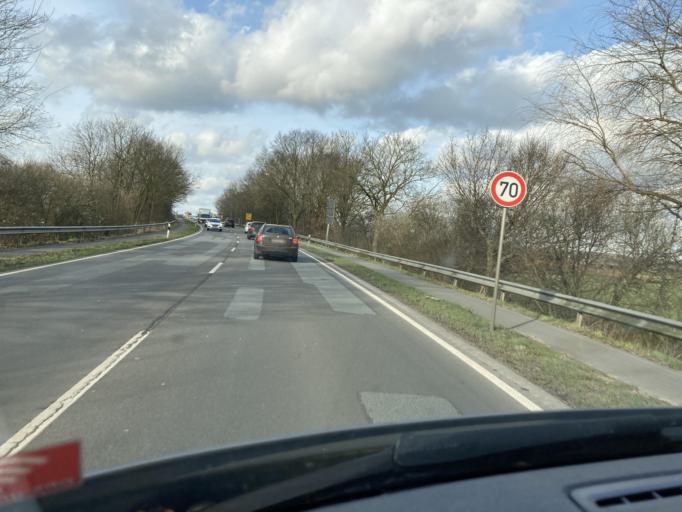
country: DE
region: Lower Saxony
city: Leer
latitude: 53.2169
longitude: 7.4849
